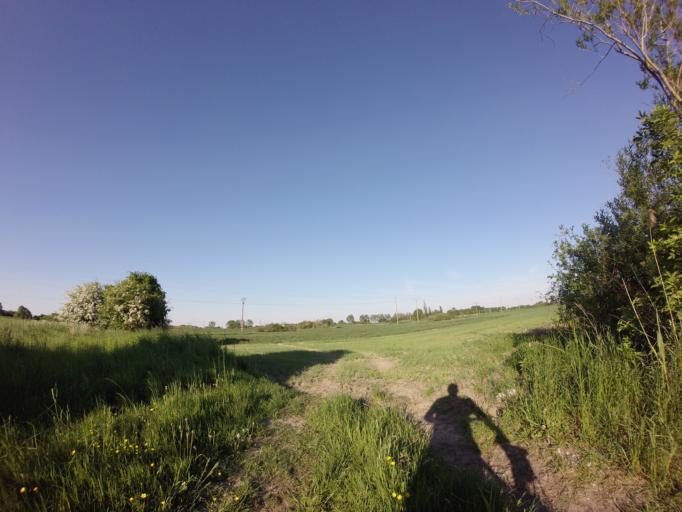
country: PL
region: West Pomeranian Voivodeship
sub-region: Powiat choszczenski
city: Choszczno
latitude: 53.1359
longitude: 15.4421
